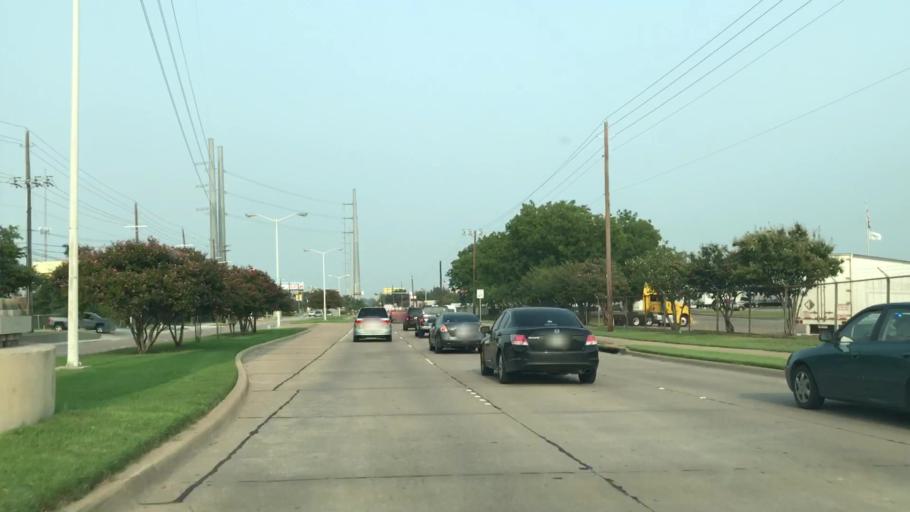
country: US
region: Texas
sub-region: Dallas County
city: Garland
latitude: 32.9090
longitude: -96.6642
